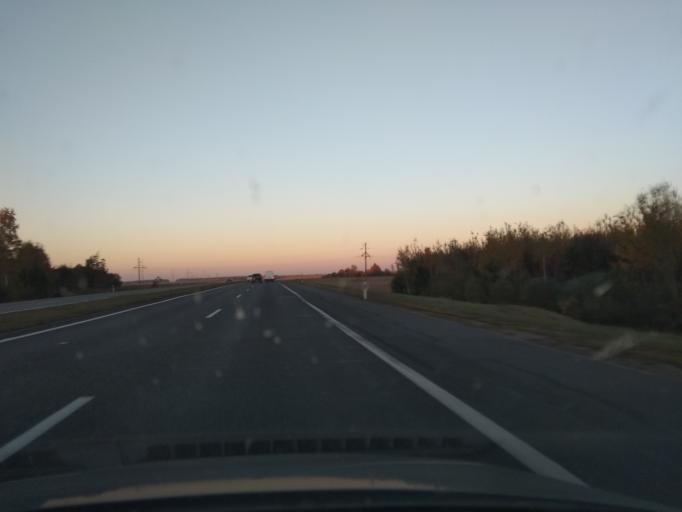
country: BY
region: Minsk
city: Haradzyeya
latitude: 53.3877
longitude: 26.5211
